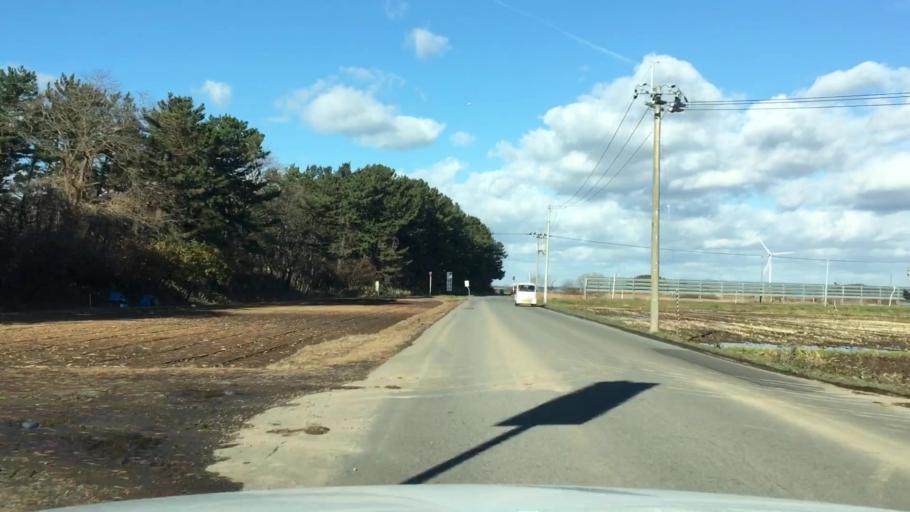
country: JP
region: Aomori
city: Shimokizukuri
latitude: 40.8481
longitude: 140.2999
